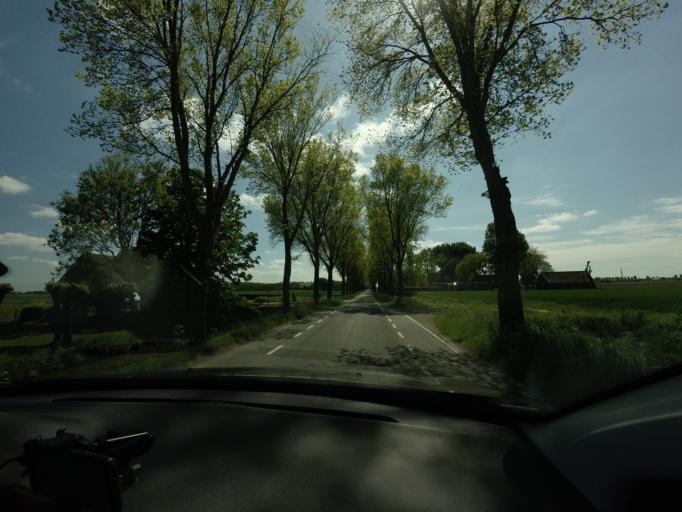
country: NL
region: North Holland
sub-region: Gemeente Beemster
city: Halfweg
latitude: 52.5701
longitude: 4.8770
